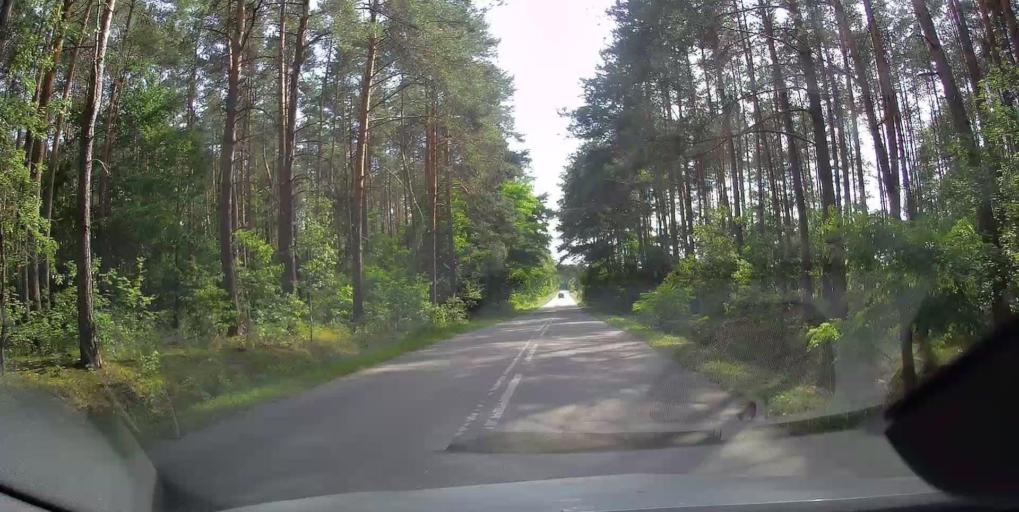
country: PL
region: Lodz Voivodeship
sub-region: Powiat opoczynski
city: Mniszkow
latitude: 51.4054
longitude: 20.0434
